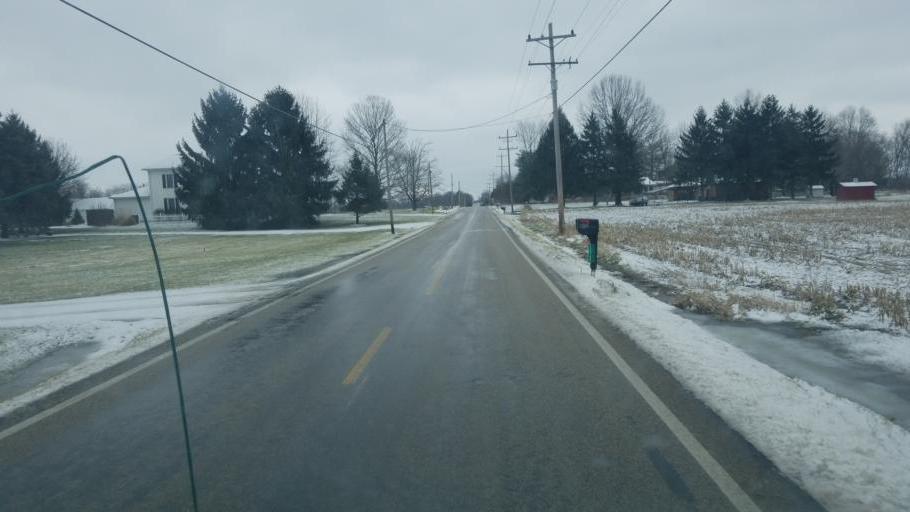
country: US
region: Ohio
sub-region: Delaware County
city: Sunbury
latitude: 40.2473
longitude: -82.7776
